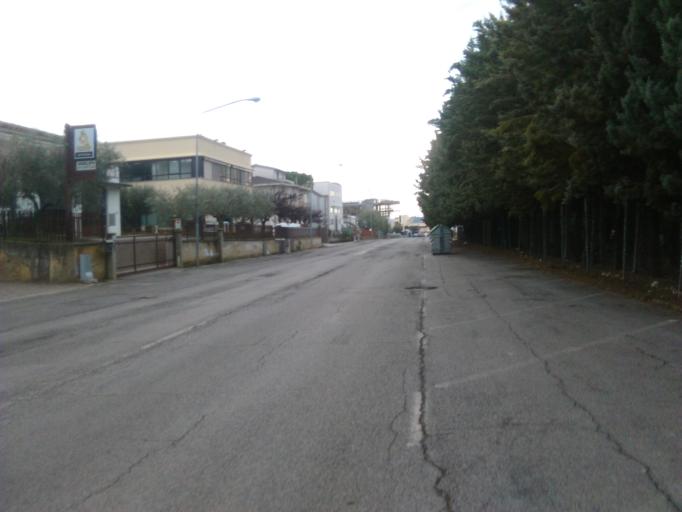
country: IT
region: Umbria
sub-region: Provincia di Perugia
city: Perugia
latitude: 43.0945
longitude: 12.3631
